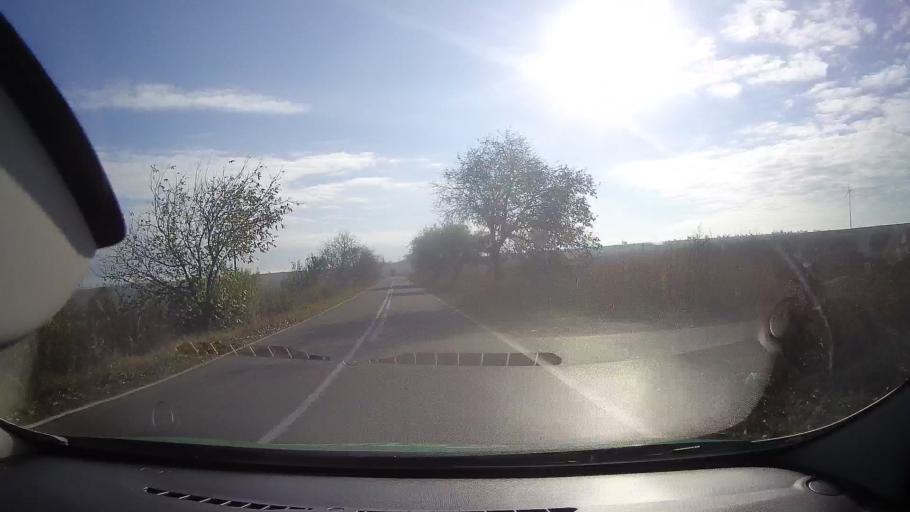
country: RO
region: Tulcea
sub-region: Comuna Mahmudia
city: Mahmudia
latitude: 45.0750
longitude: 29.0808
